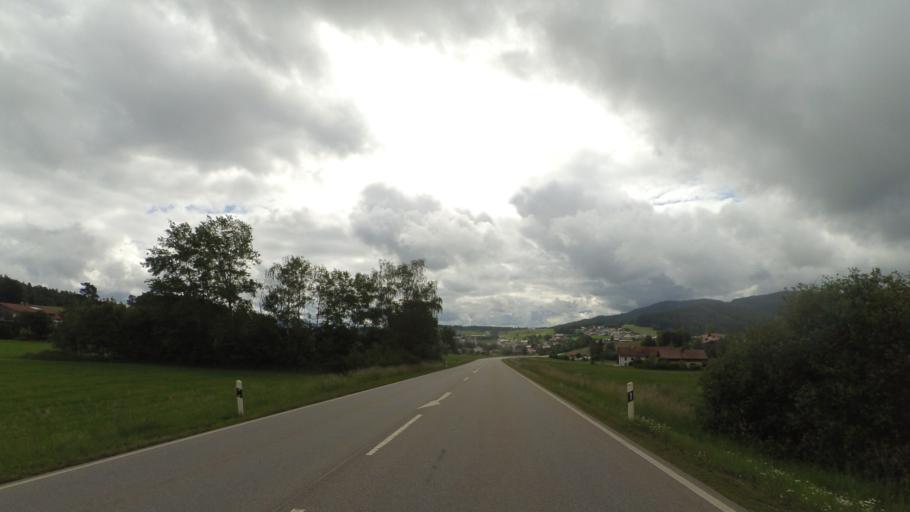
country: DE
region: Bavaria
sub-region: Lower Bavaria
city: Prackenbach
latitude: 49.0980
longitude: 12.8154
